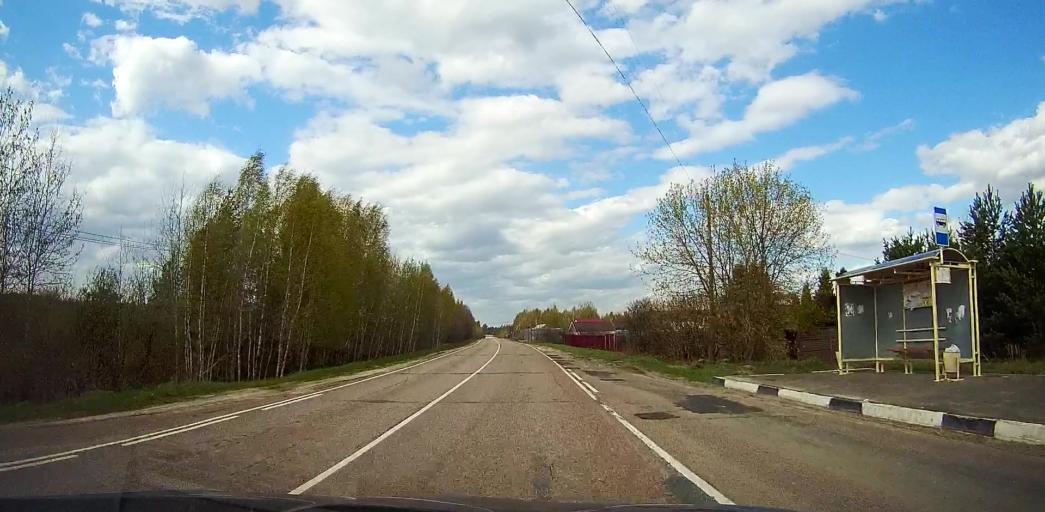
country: RU
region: Moskovskaya
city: Rakhmanovo
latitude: 55.6708
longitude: 38.6461
